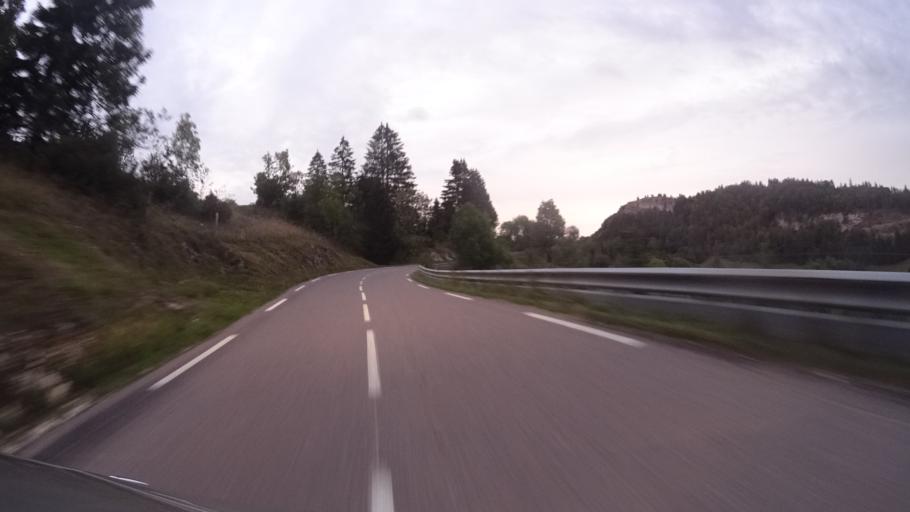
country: CH
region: Vaud
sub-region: Jura-Nord vaudois District
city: Le Chenit
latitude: 46.6701
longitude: 6.1018
